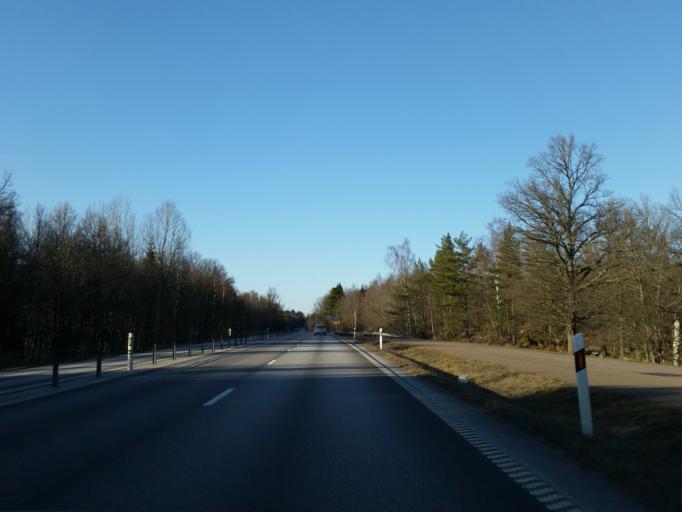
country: SE
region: Kalmar
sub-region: Oskarshamns Kommun
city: Oskarshamn
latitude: 57.3007
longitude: 16.4612
